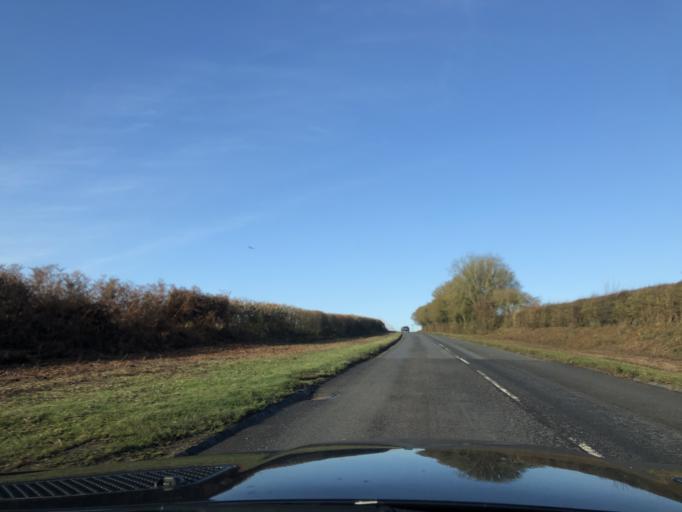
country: GB
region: England
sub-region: Buckinghamshire
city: Marlow
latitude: 51.5968
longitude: -0.7675
